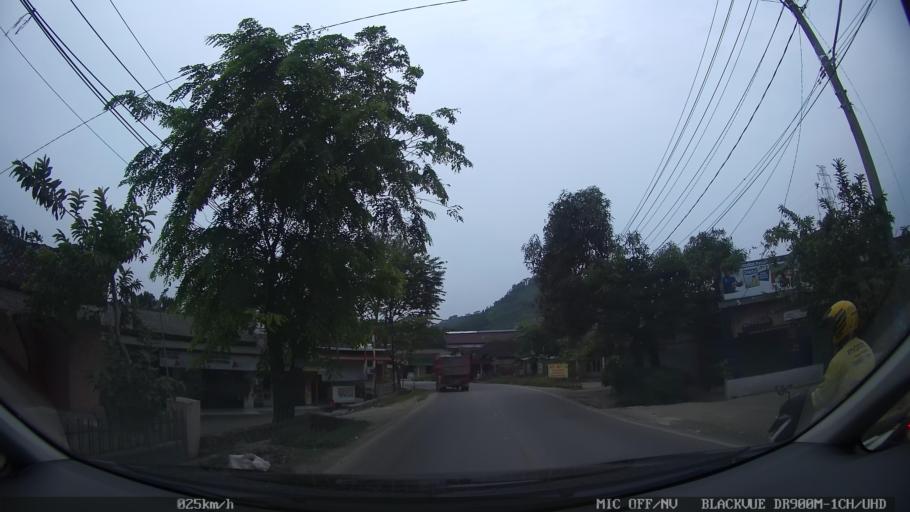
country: ID
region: Lampung
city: Panjang
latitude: -5.4190
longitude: 105.3364
